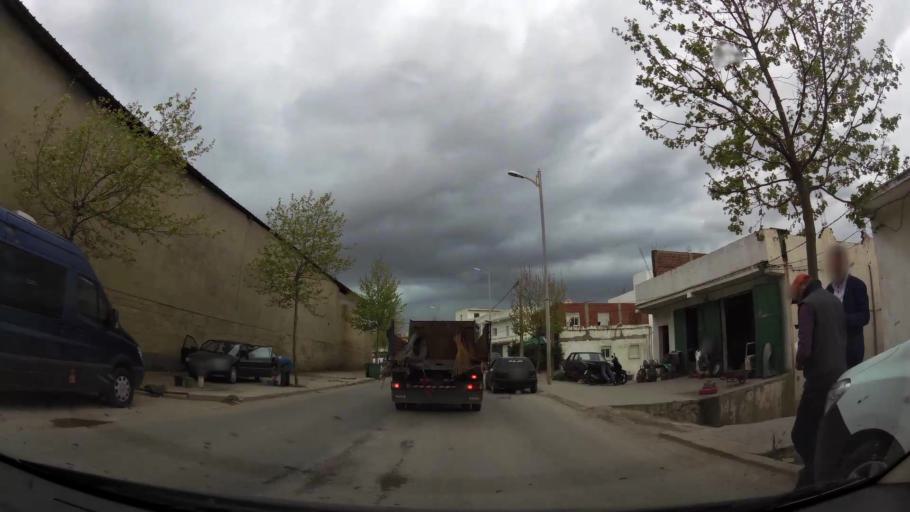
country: MA
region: Tanger-Tetouan
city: Tetouan
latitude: 35.5551
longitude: -5.3995
